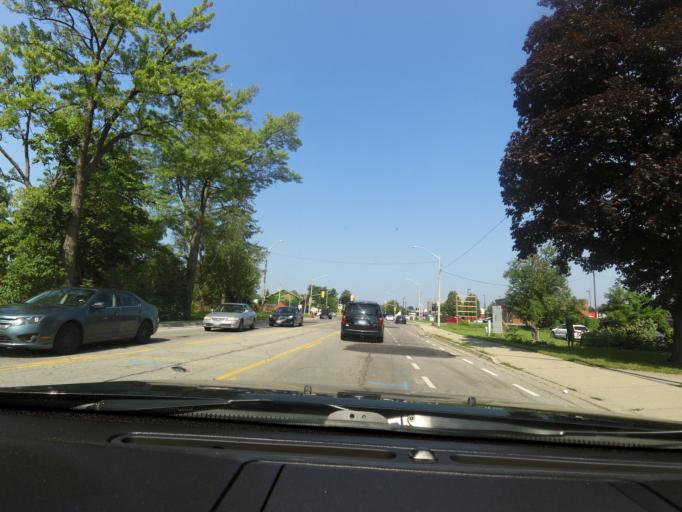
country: CA
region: Ontario
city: Hamilton
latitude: 43.2108
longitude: -79.8879
